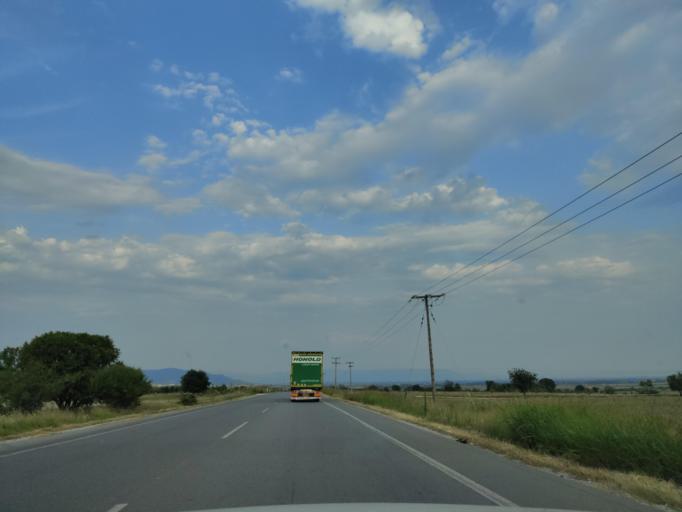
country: GR
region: East Macedonia and Thrace
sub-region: Nomos Dramas
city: Petroussa
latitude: 41.1745
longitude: 24.0164
